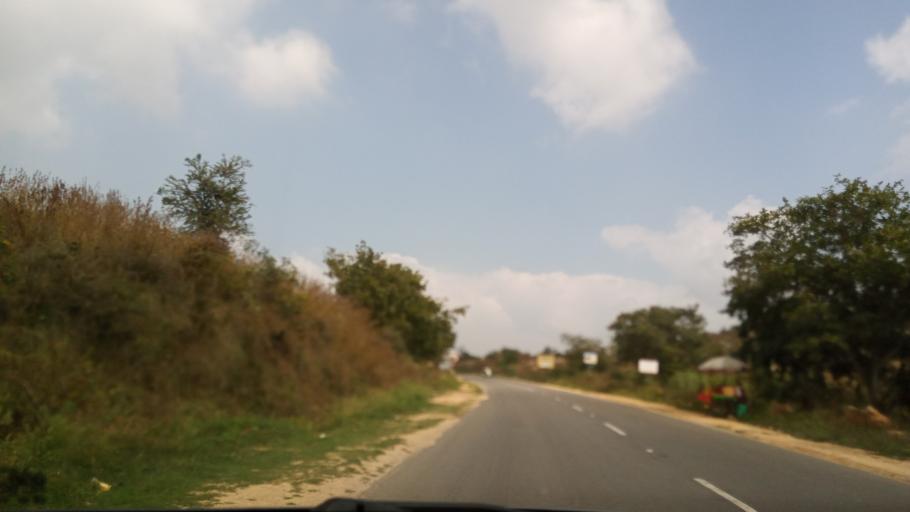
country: IN
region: Andhra Pradesh
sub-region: Chittoor
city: Madanapalle
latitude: 13.5843
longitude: 78.5221
